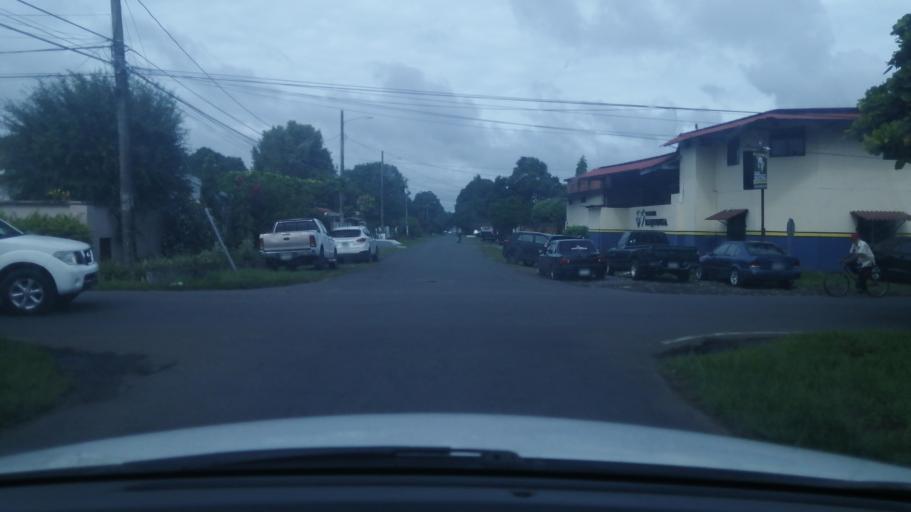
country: PA
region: Chiriqui
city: David
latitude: 8.4363
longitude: -82.4301
